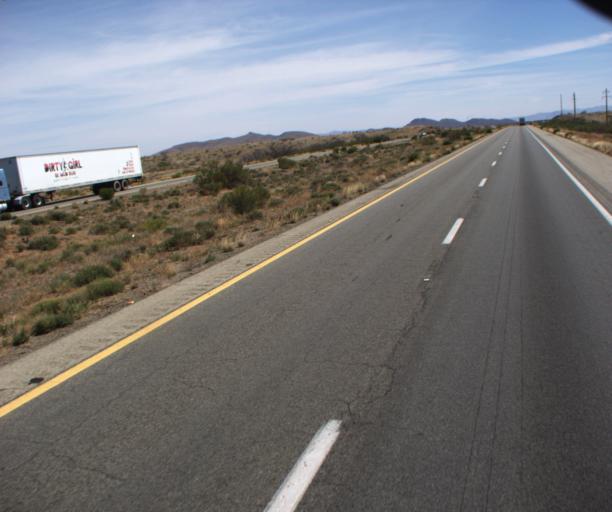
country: US
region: Arizona
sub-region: Cochise County
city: Willcox
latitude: 32.3569
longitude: -109.6946
